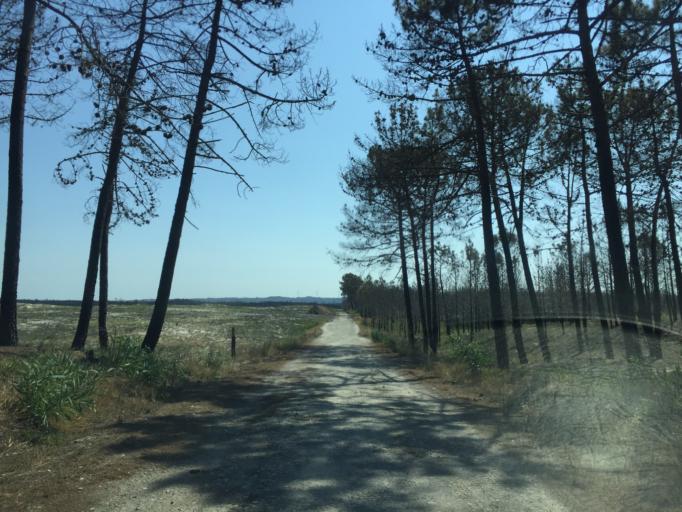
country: PT
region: Coimbra
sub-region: Figueira da Foz
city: Alhadas
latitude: 40.2640
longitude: -8.8332
